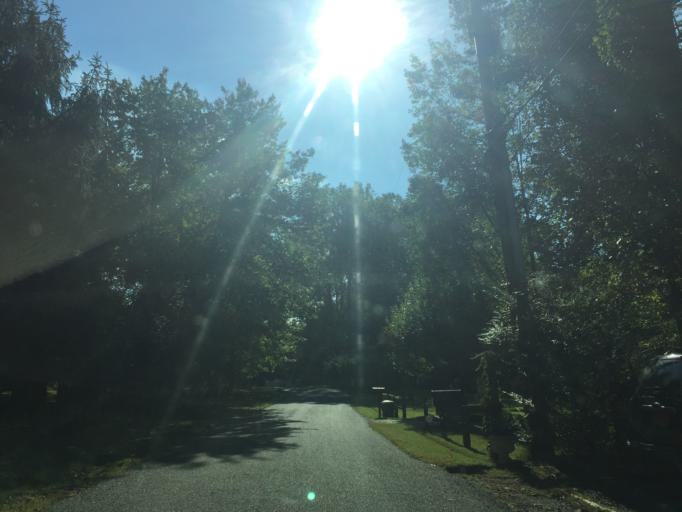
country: US
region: Maryland
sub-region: Baltimore County
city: Perry Hall
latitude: 39.4269
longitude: -76.4706
